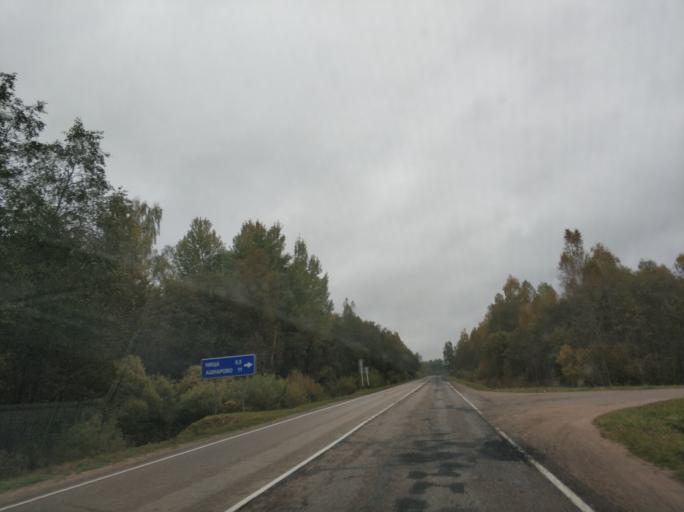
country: BY
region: Vitebsk
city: Rasony
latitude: 56.0667
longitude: 28.7143
